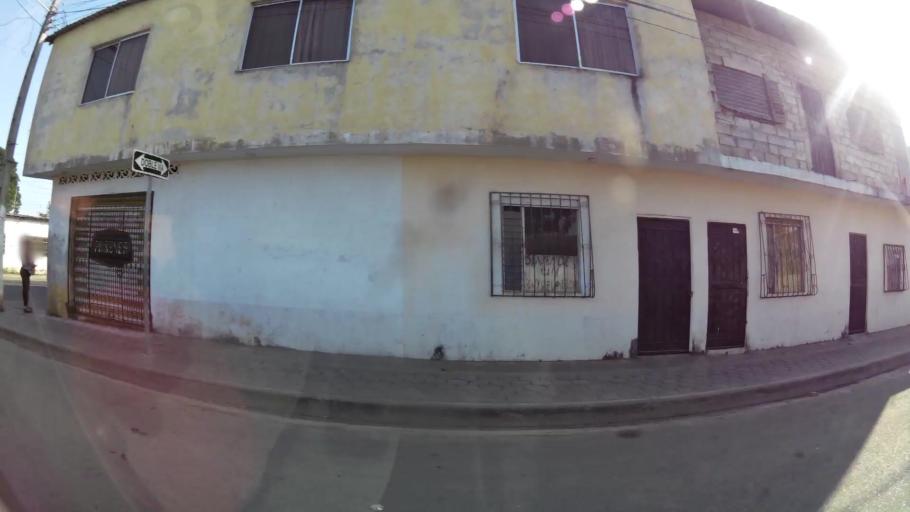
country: EC
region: Guayas
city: Eloy Alfaro
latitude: -2.1863
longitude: -79.8468
